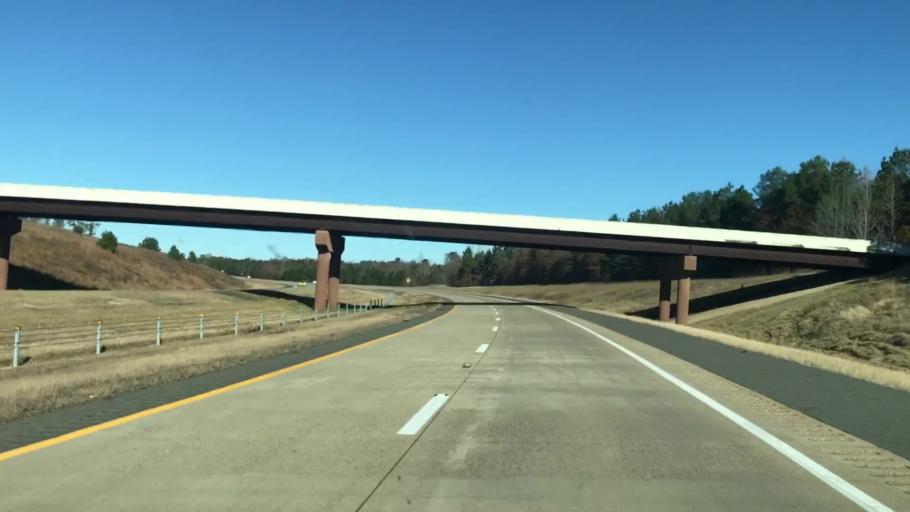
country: US
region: Texas
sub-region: Bowie County
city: Texarkana
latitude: 33.2688
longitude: -93.8978
